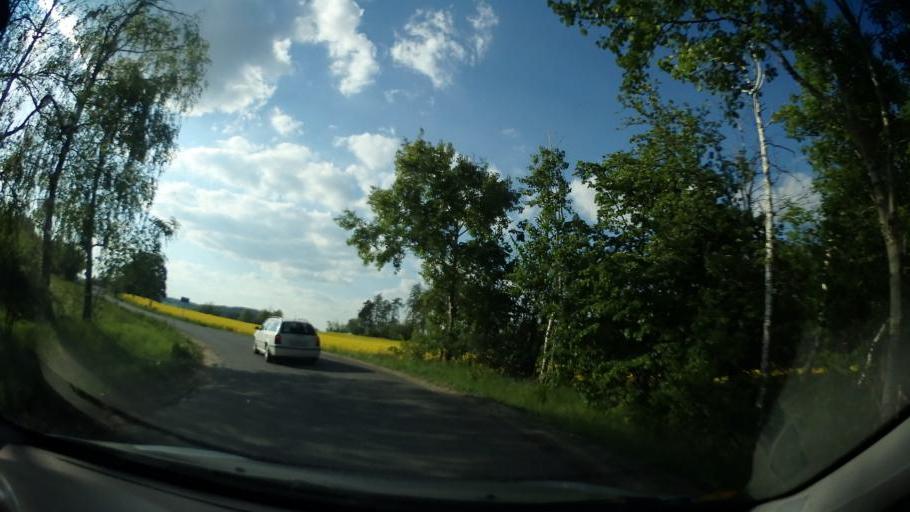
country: CZ
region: Vysocina
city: Budisov
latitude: 49.3114
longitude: 15.9751
